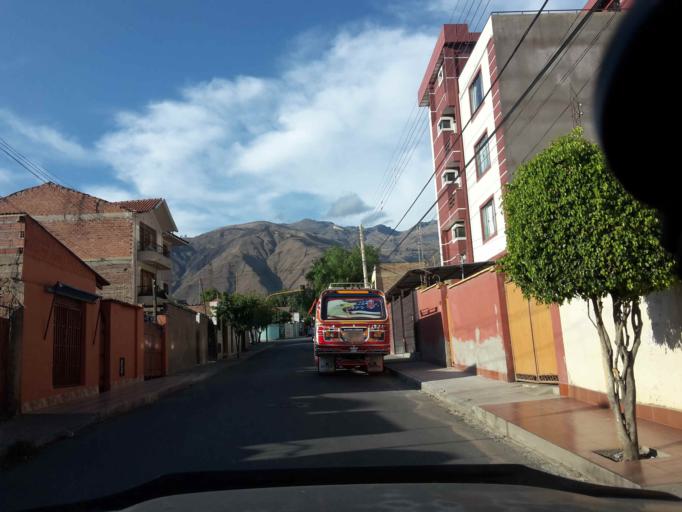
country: BO
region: Cochabamba
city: Cochabamba
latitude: -17.3474
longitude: -66.1954
